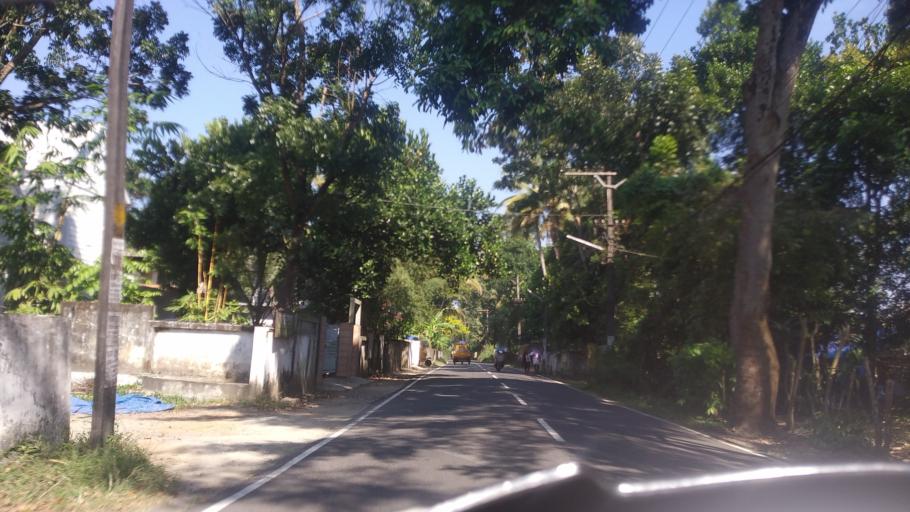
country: IN
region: Kerala
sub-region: Ernakulam
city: Elur
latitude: 10.1117
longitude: 76.2487
